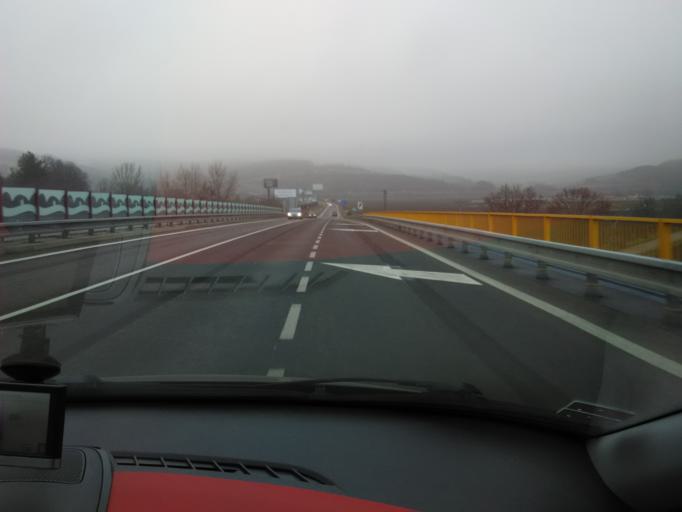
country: SK
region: Trenciansky
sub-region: Okres Trencin
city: Trencin
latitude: 48.8956
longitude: 18.0017
